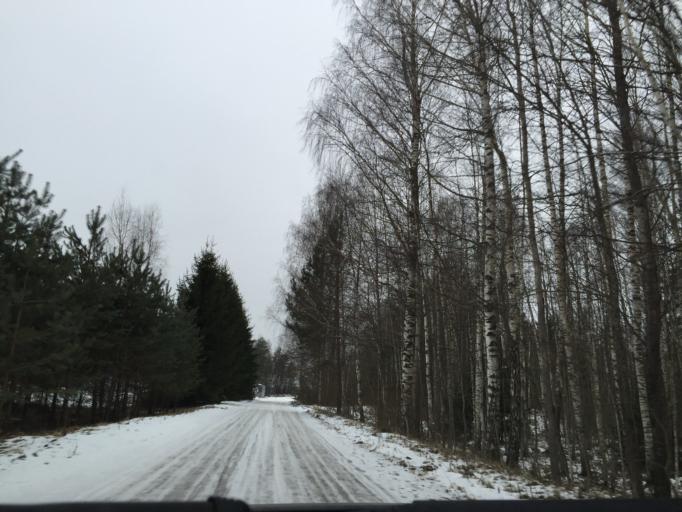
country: LV
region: Saulkrastu
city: Saulkrasti
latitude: 57.2398
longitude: 24.5091
